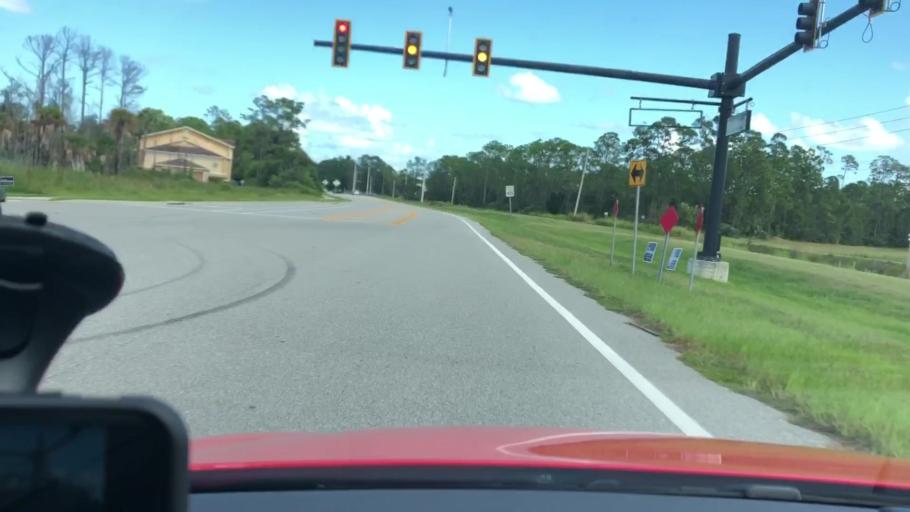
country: US
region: Florida
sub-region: Volusia County
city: Holly Hill
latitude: 29.2010
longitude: -81.0908
